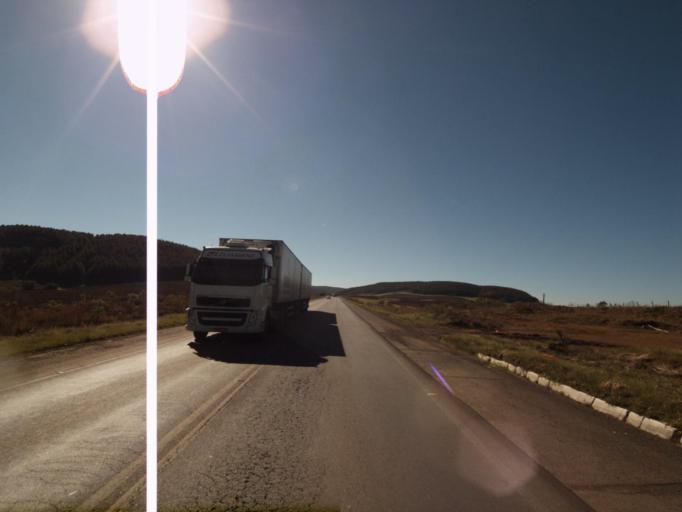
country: BR
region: Parana
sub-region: Palmas
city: Palmas
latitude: -26.6801
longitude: -51.5578
